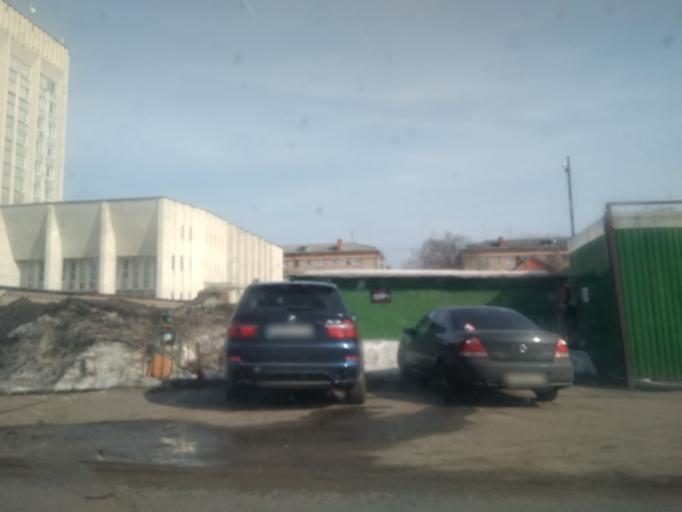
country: RU
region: Moskovskaya
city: Zhukovskiy
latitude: 55.5946
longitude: 38.1142
